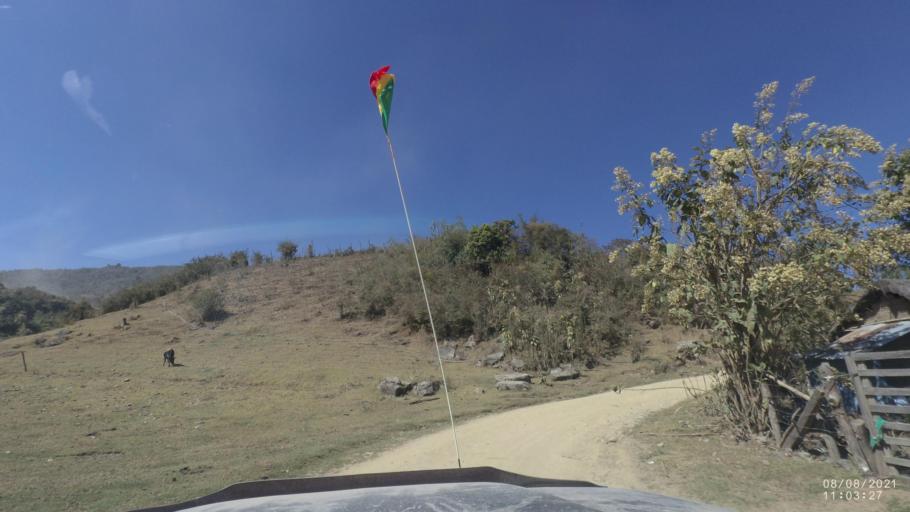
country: BO
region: Cochabamba
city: Colchani
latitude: -16.7544
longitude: -66.6860
